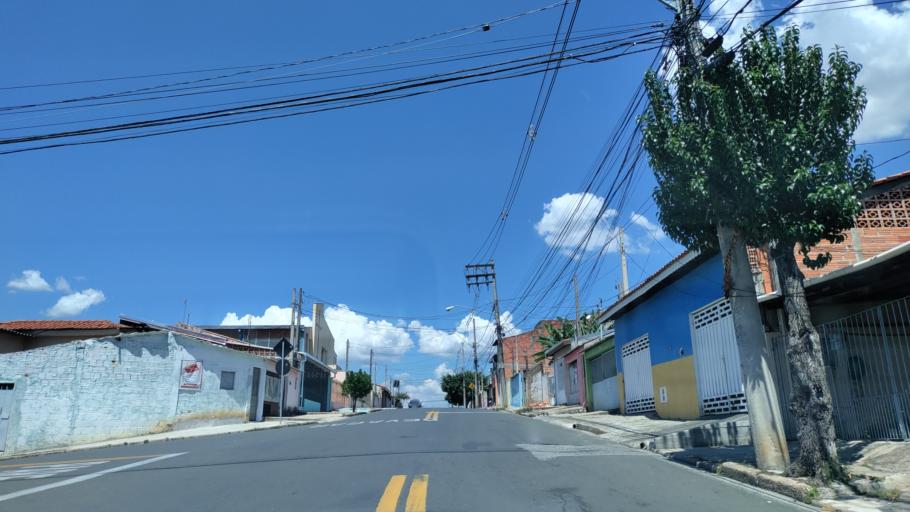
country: BR
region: Sao Paulo
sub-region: Sorocaba
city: Sorocaba
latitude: -23.4636
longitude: -47.4674
